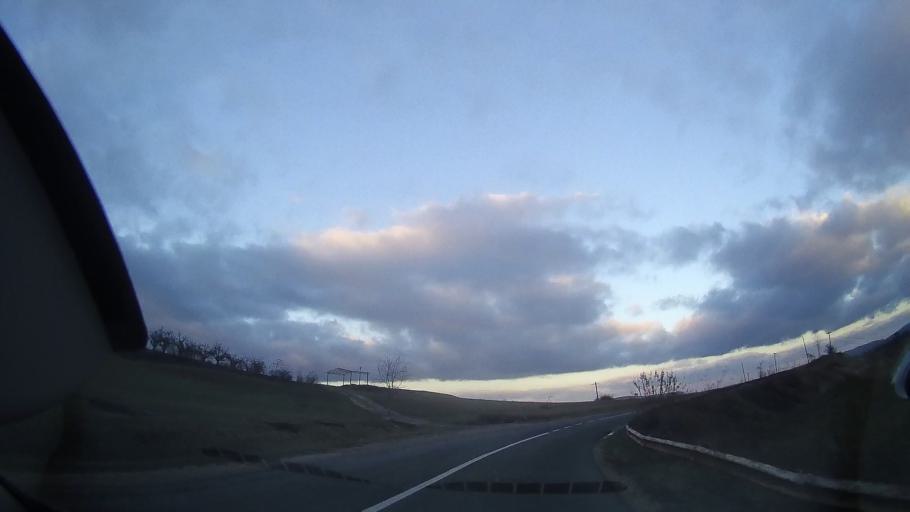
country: RO
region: Cluj
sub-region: Comuna Manastireni
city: Manastireni
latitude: 46.7874
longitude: 23.0934
